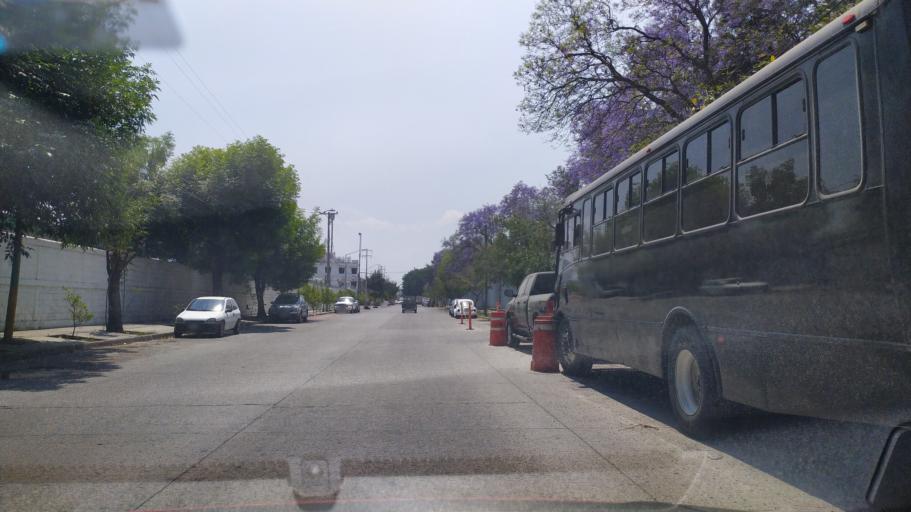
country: MX
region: Jalisco
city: Guadalajara
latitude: 20.6475
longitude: -103.3670
